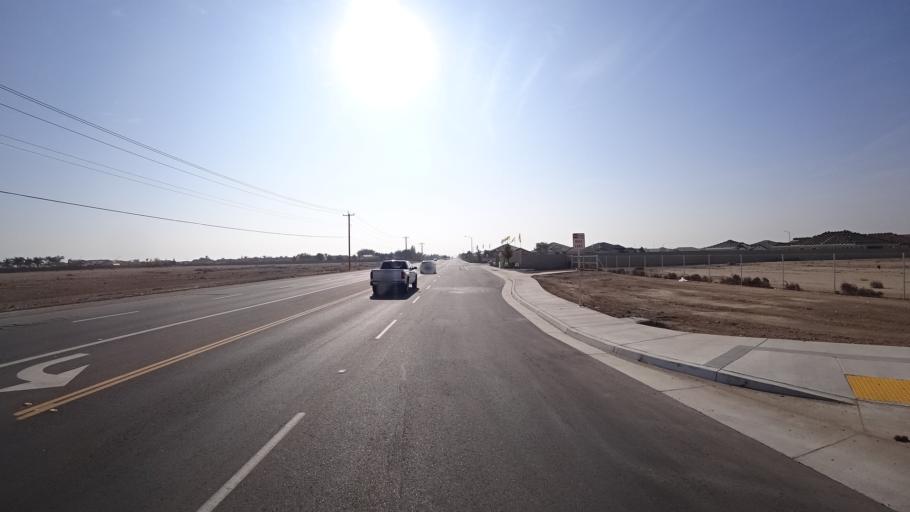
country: US
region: California
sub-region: Kern County
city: Greenacres
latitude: 35.2947
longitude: -119.1100
